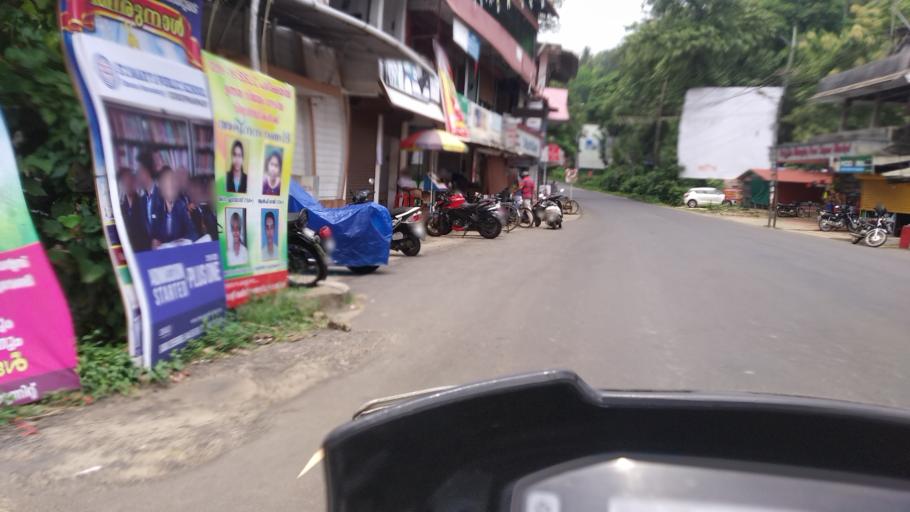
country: IN
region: Kerala
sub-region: Ernakulam
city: Perumpavur
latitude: 10.1017
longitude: 76.5416
